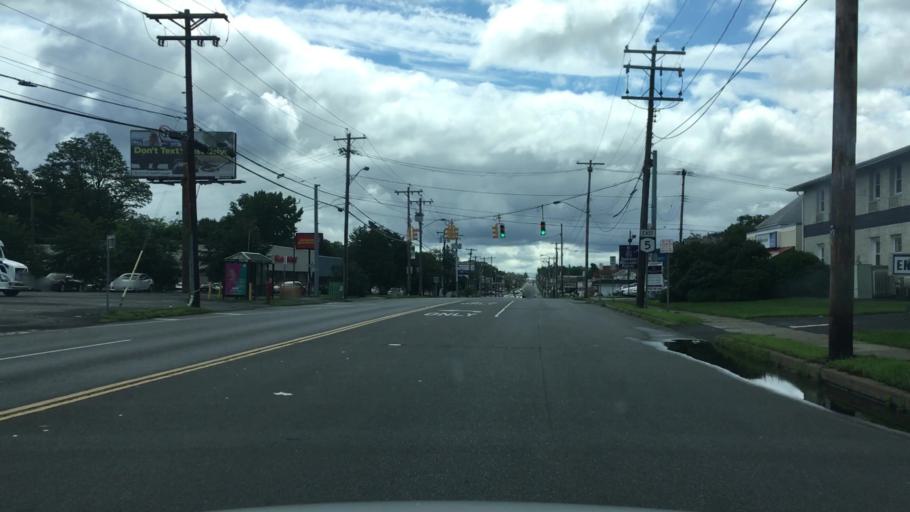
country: US
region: New York
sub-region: Schenectady County
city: Schenectady
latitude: 42.7851
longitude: -73.9094
